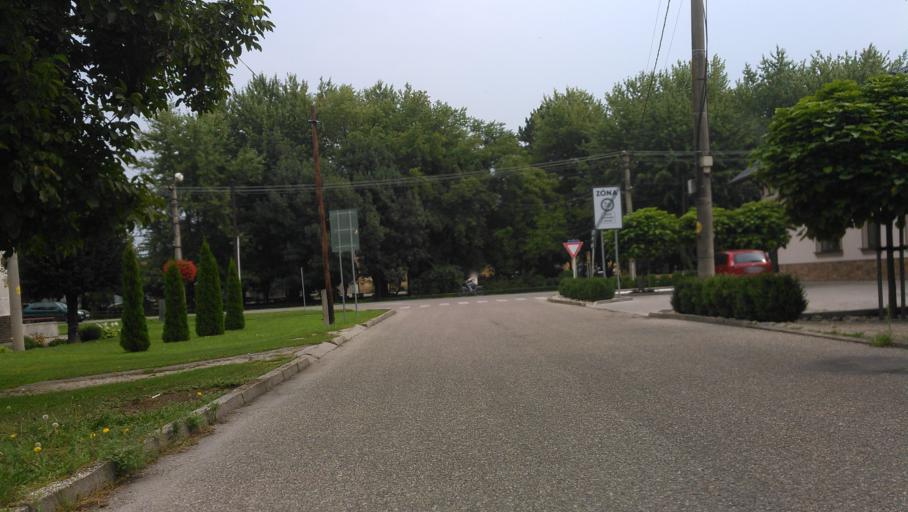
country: SK
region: Nitriansky
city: Kolarovo
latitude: 47.9189
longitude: 17.9923
